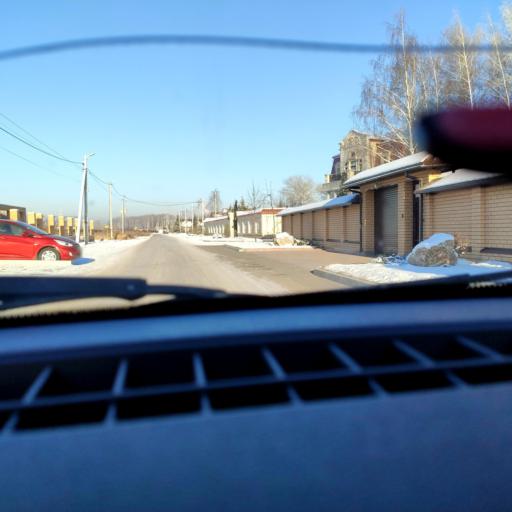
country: RU
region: Bashkortostan
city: Ufa
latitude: 54.6626
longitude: 55.9250
